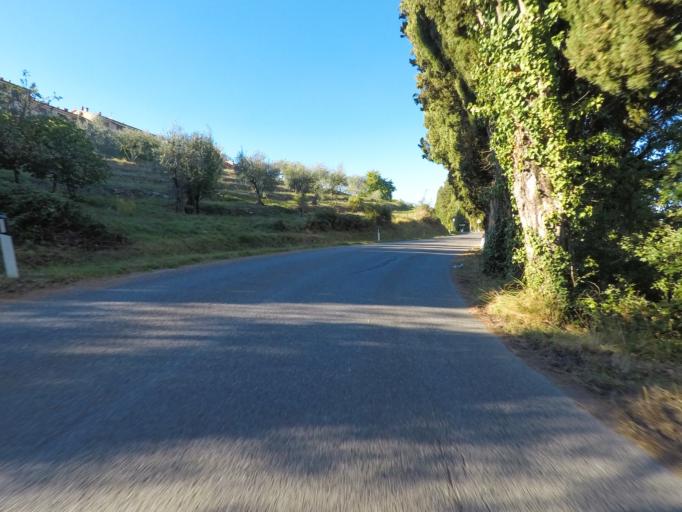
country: IT
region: Tuscany
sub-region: Provincia di Siena
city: Radda in Chianti
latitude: 43.4151
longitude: 11.3489
